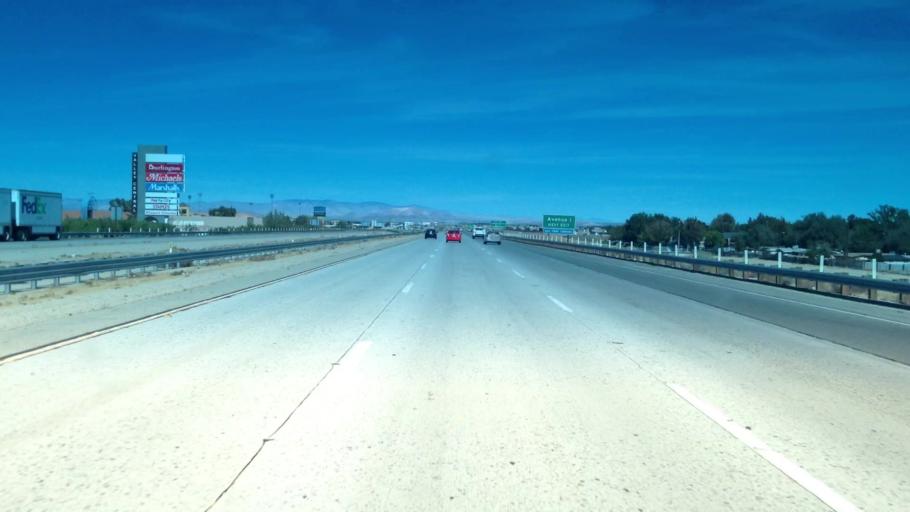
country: US
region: California
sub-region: Los Angeles County
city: Lancaster
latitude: 34.6933
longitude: -118.1698
